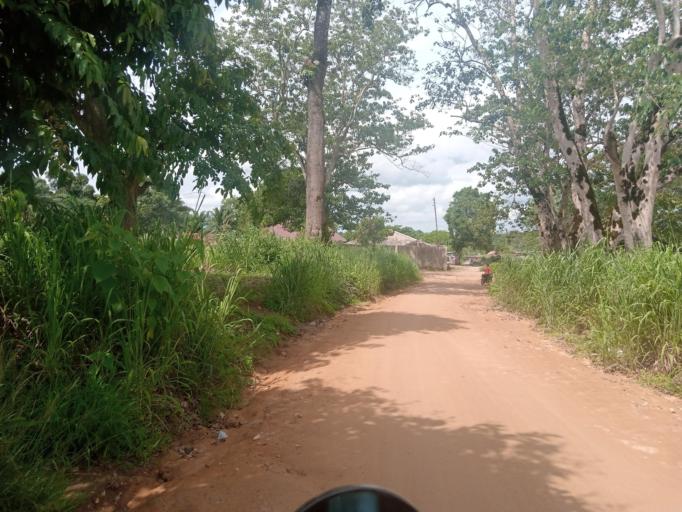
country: SL
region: Southern Province
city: Bo
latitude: 7.9661
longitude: -11.7560
